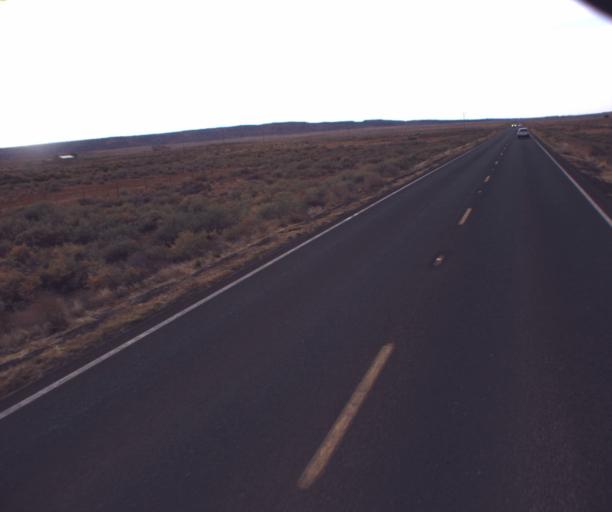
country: US
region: Arizona
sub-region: Apache County
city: Ganado
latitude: 35.8091
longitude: -109.6110
